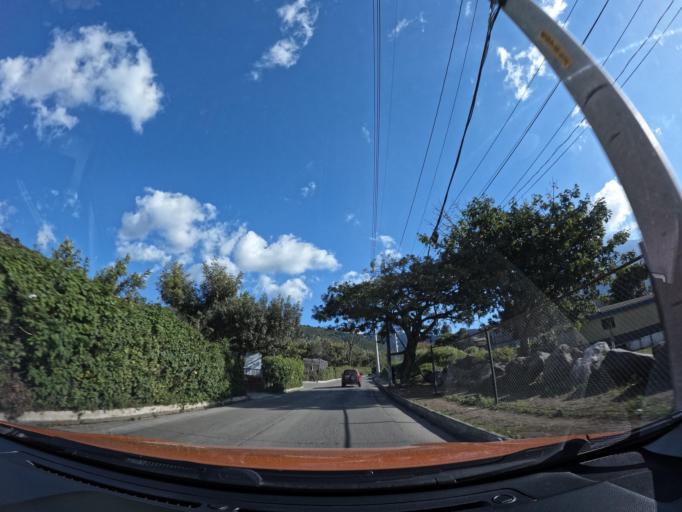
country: GT
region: Sacatepequez
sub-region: Municipio de Santa Maria de Jesus
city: Santa Maria de Jesus
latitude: 14.5336
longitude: -90.7287
